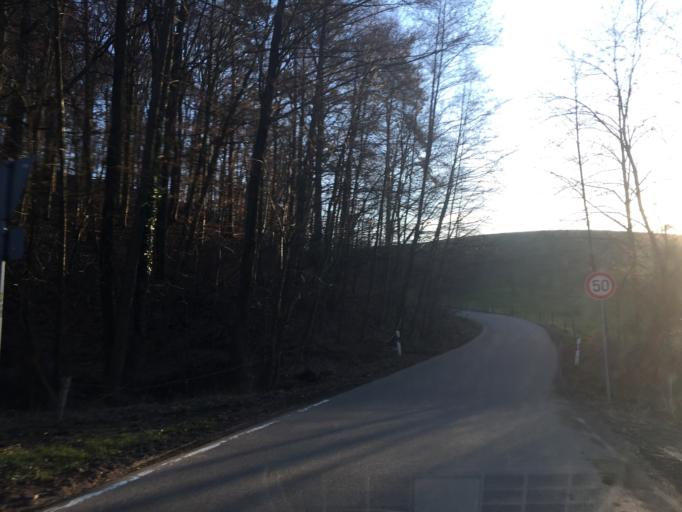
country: DE
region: Hesse
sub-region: Regierungsbezirk Darmstadt
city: Birkenau
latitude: 49.5183
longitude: 8.7082
